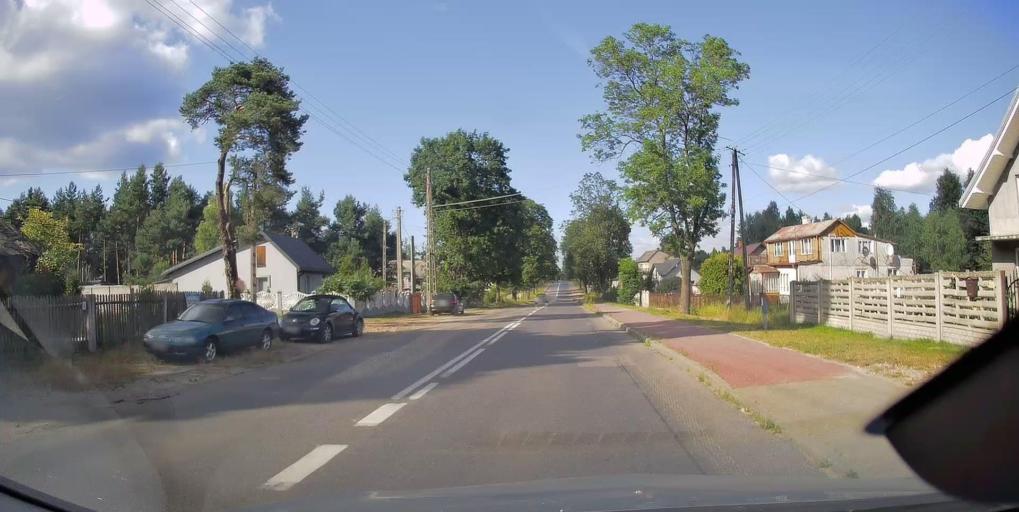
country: PL
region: Swietokrzyskie
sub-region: Powiat skarzyski
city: Suchedniow
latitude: 51.0275
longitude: 20.8372
